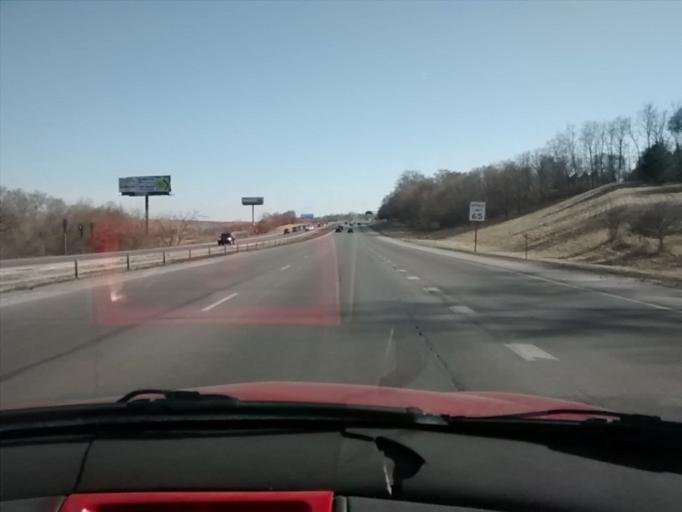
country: US
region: Nebraska
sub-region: Douglas County
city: Omaha
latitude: 41.1925
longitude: -95.9404
